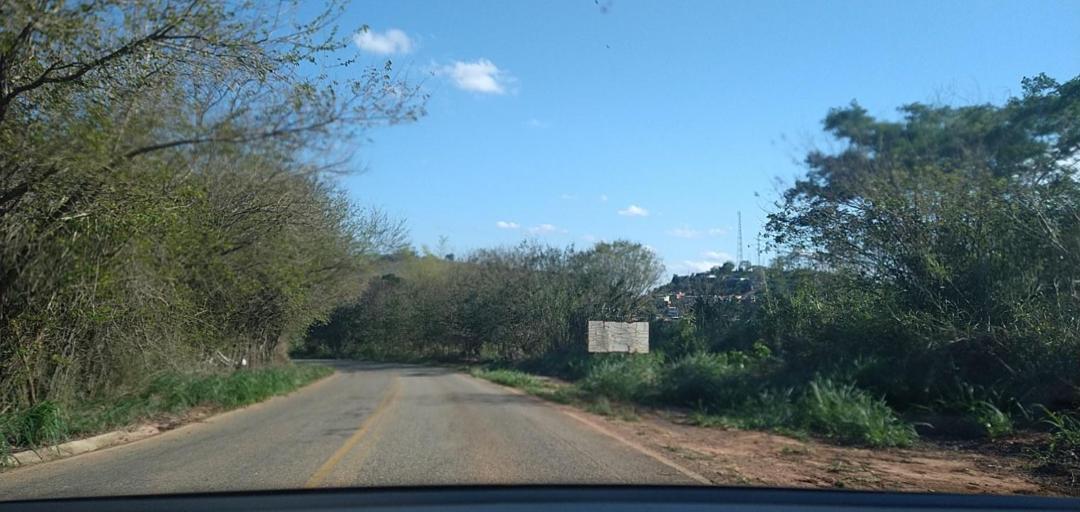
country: BR
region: Minas Gerais
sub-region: Ponte Nova
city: Ponte Nova
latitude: -20.2393
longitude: -42.8977
